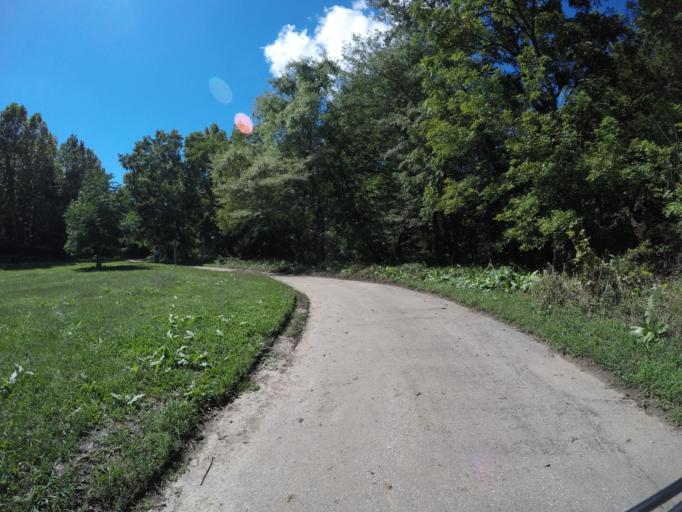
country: US
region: Kansas
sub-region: Johnson County
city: Lenexa
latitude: 38.9003
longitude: -94.7484
